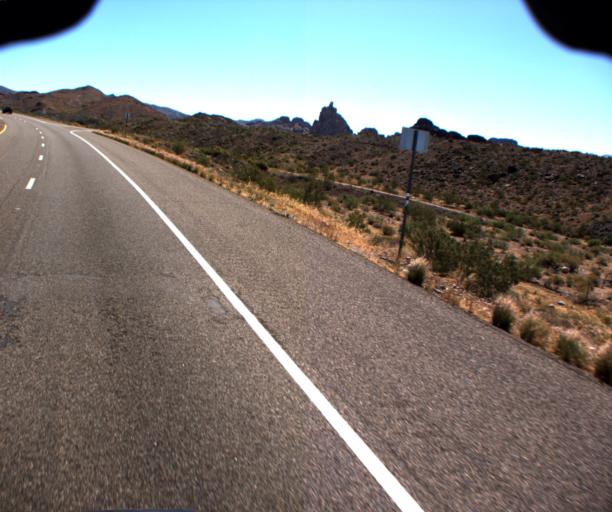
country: US
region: Nevada
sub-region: Clark County
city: Laughlin
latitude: 35.1854
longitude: -114.4563
